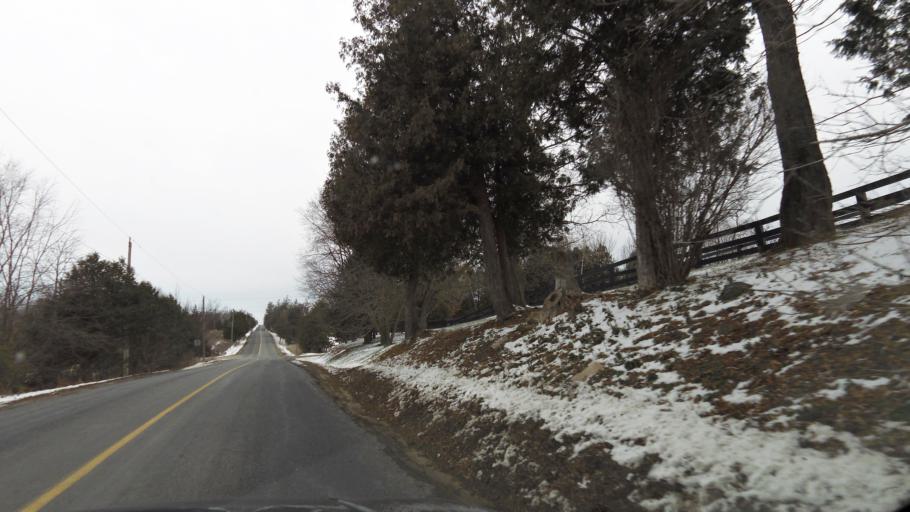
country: CA
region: Ontario
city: Bradford West Gwillimbury
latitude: 43.9611
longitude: -79.6411
